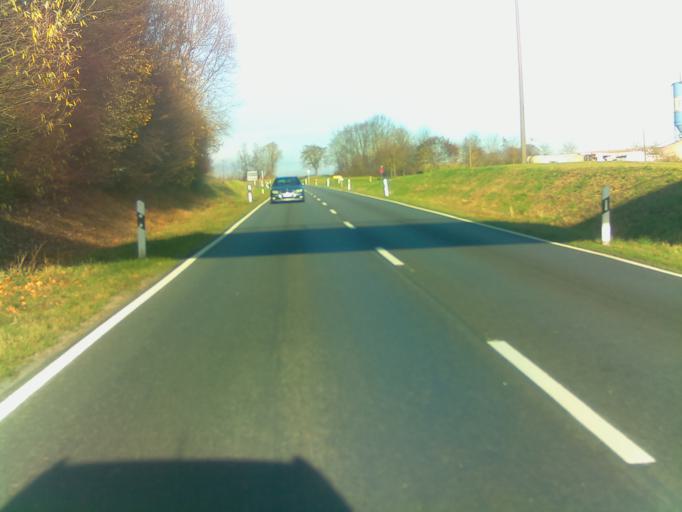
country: DE
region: Bavaria
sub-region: Regierungsbezirk Unterfranken
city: Kreuzwertheim
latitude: 49.8028
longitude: 9.5524
